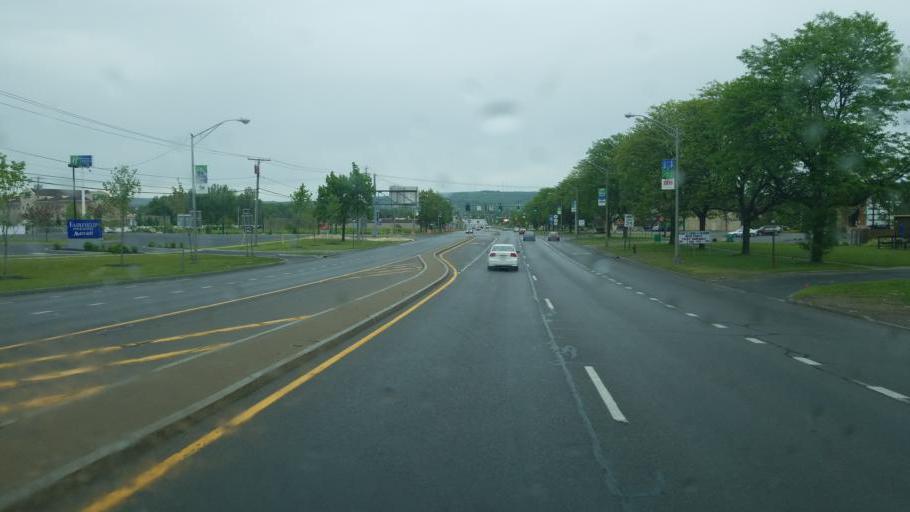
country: US
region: New York
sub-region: Oneida County
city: Utica
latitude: 43.1068
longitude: -75.2220
